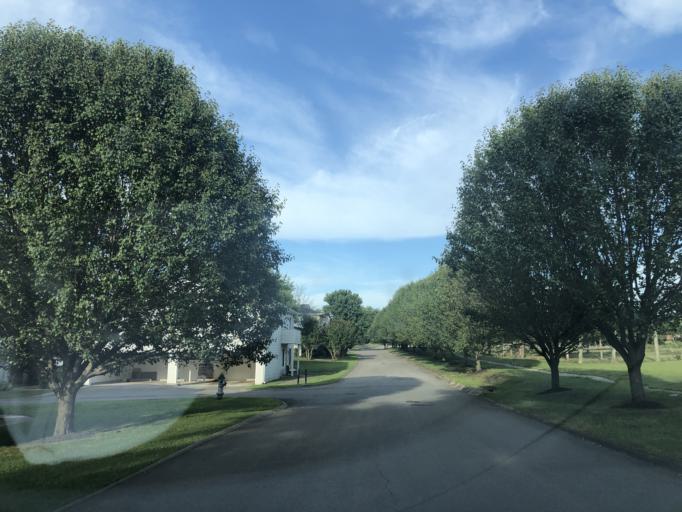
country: US
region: Tennessee
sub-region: Davidson County
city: Belle Meade
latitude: 36.0717
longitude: -86.9379
